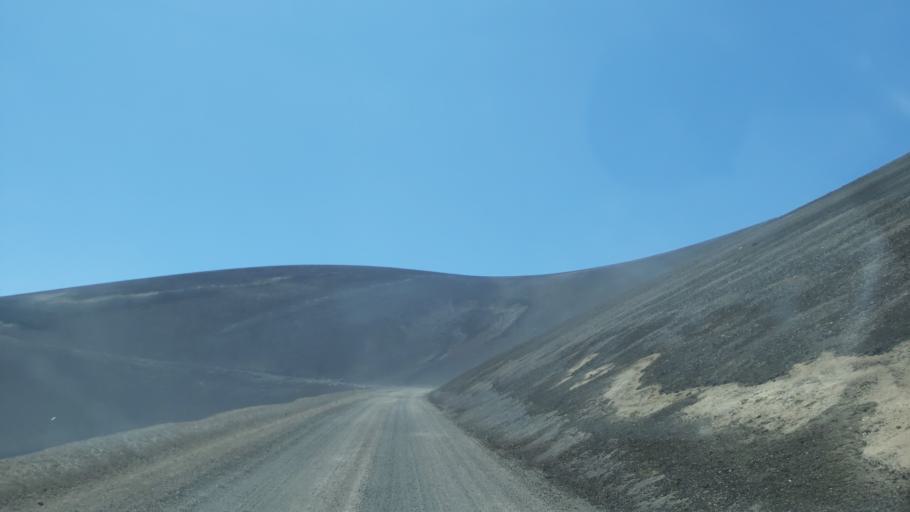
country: CL
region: Araucania
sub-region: Provincia de Cautin
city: Vilcun
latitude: -38.3917
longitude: -71.5454
